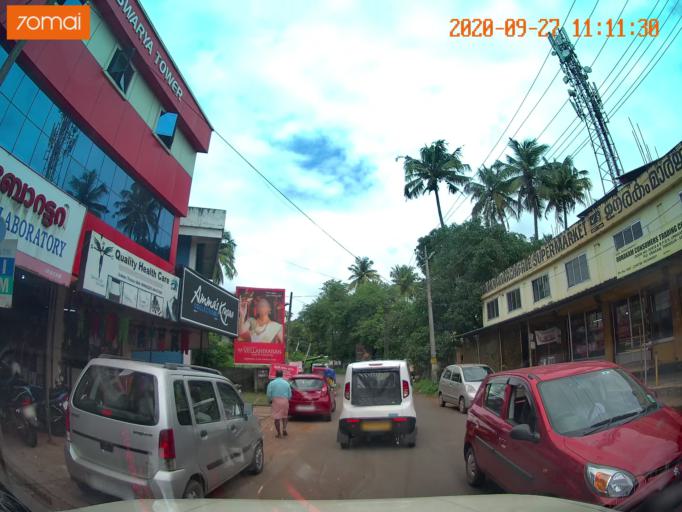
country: IN
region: Kerala
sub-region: Thrissur District
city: Thanniyam
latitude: 10.4319
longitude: 76.2165
